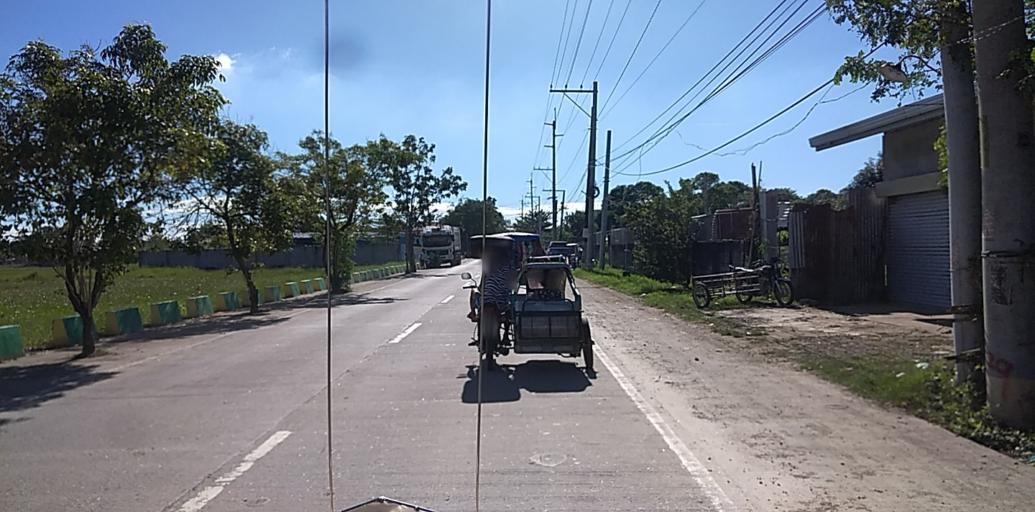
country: PH
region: Central Luzon
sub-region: Province of Pampanga
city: San Carlos
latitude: 15.0584
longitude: 120.7749
